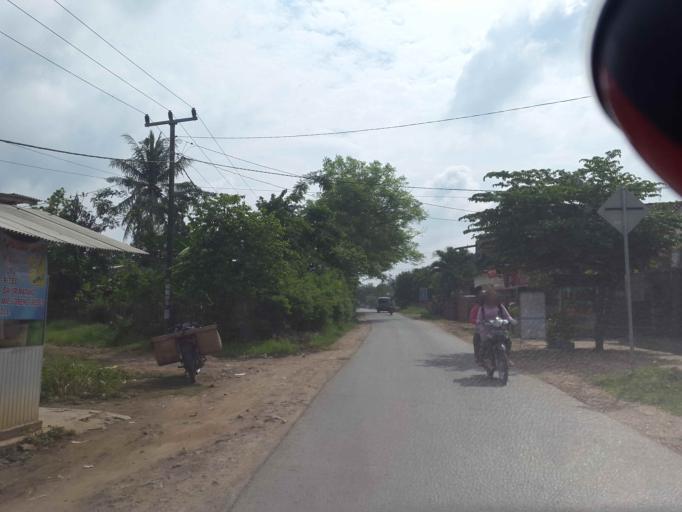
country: ID
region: Lampung
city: Natar
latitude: -5.3101
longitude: 105.2086
